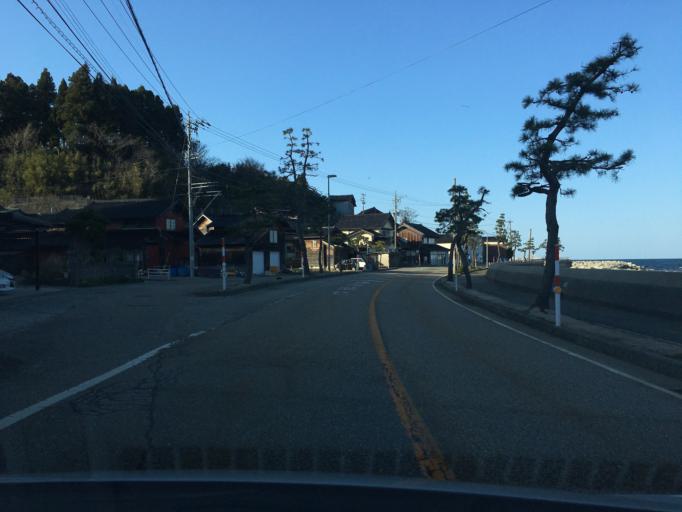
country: JP
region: Ishikawa
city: Nanao
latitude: 36.9662
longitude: 137.0556
